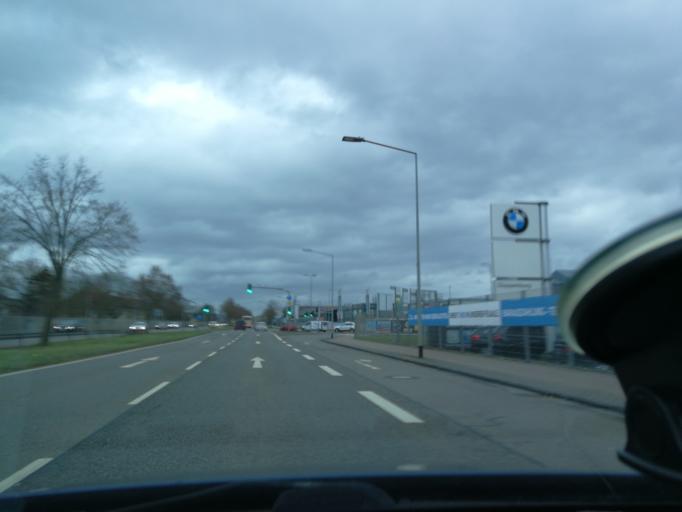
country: DE
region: Rheinland-Pfalz
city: Trier
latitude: 49.7313
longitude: 6.6068
